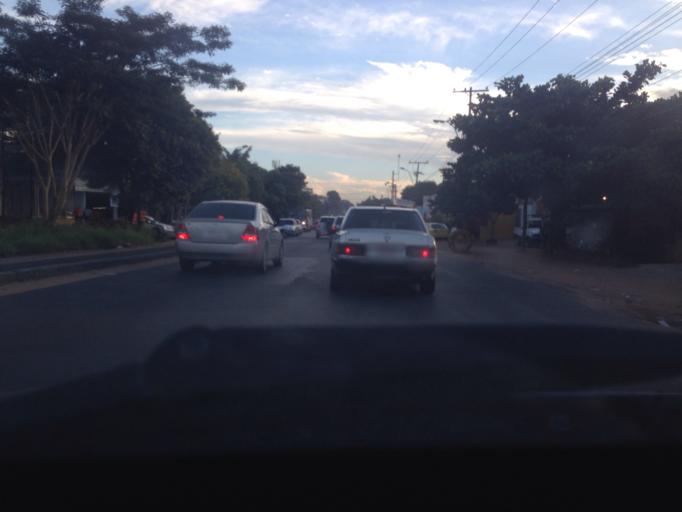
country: PY
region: Central
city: Lambare
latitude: -25.3427
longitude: -57.5869
